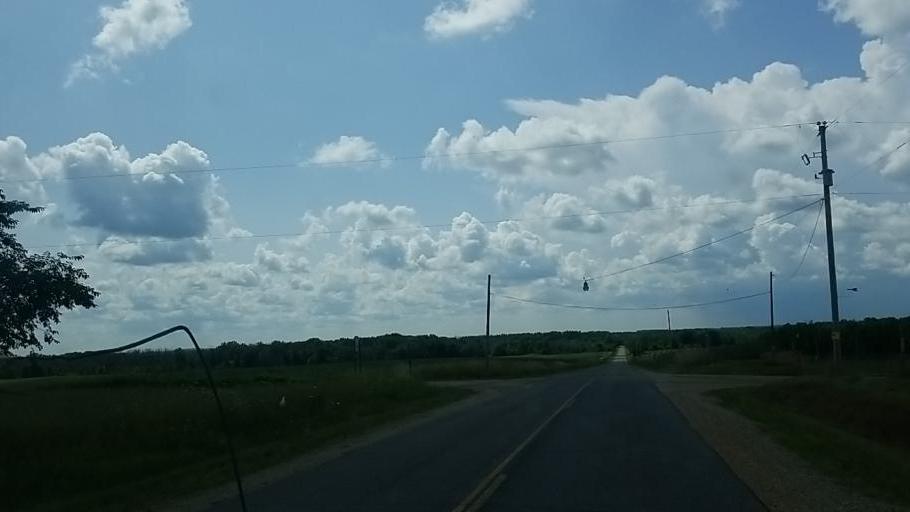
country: US
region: Michigan
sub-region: Muskegon County
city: Ravenna
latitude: 43.2209
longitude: -85.8798
